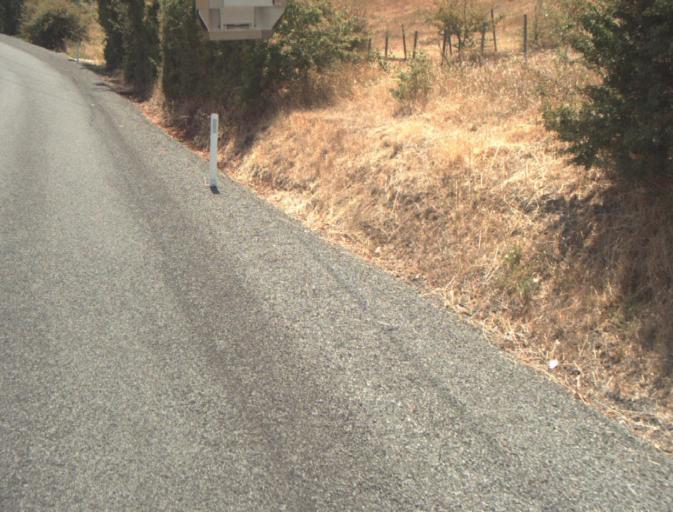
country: AU
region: Tasmania
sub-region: Launceston
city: Newstead
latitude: -41.4699
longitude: 147.1883
